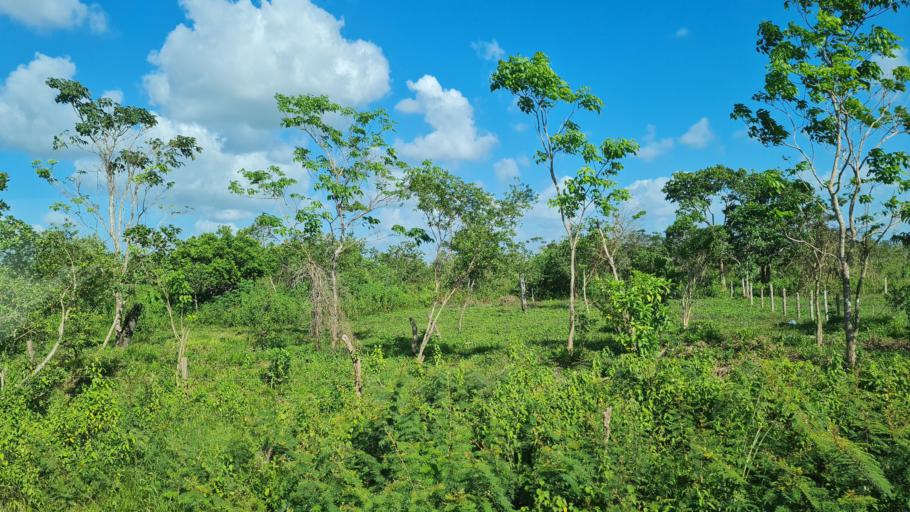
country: NI
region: Atlantico Norte (RAAN)
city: Bonanza
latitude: 13.9936
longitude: -84.1728
